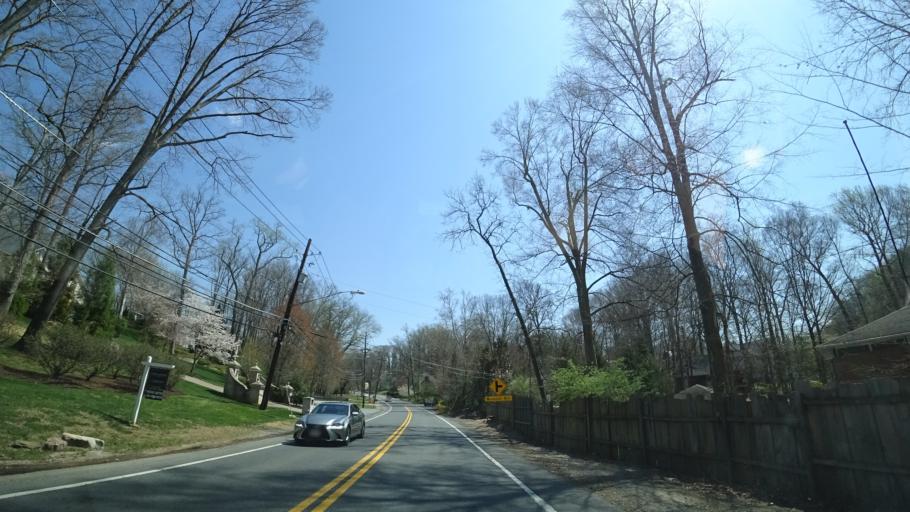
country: US
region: Maryland
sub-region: Montgomery County
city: Bethesda
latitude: 38.9971
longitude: -77.1301
